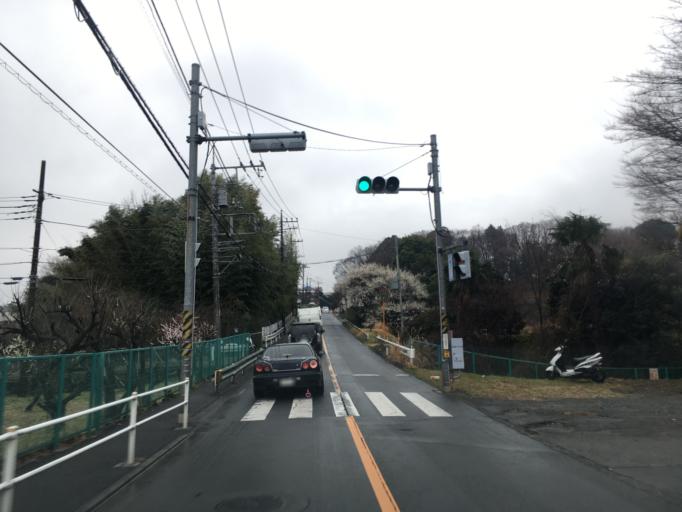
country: JP
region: Tokyo
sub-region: Machida-shi
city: Machida
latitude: 35.5755
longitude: 139.4286
